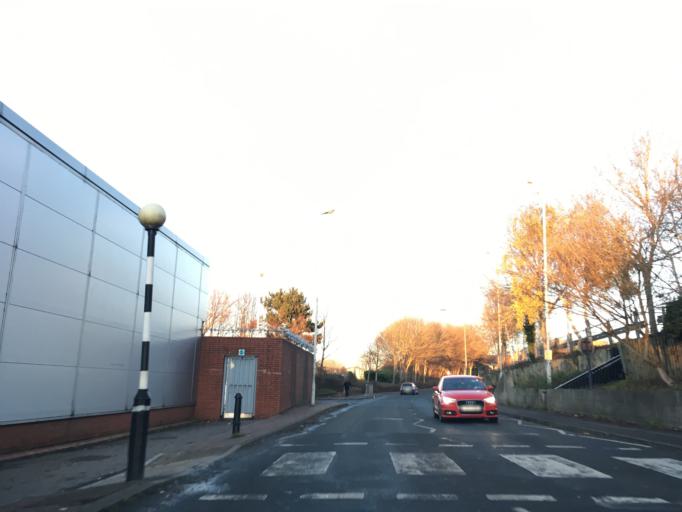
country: GB
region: England
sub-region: South Gloucestershire
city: Stoke Gifford
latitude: 51.5075
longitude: -2.5523
